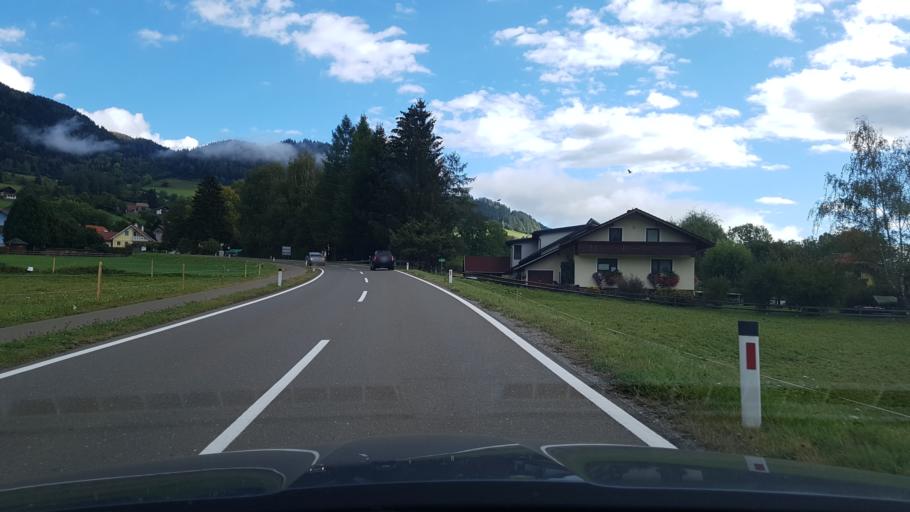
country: AT
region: Styria
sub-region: Politischer Bezirk Murau
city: Schoder
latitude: 47.1871
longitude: 14.1269
